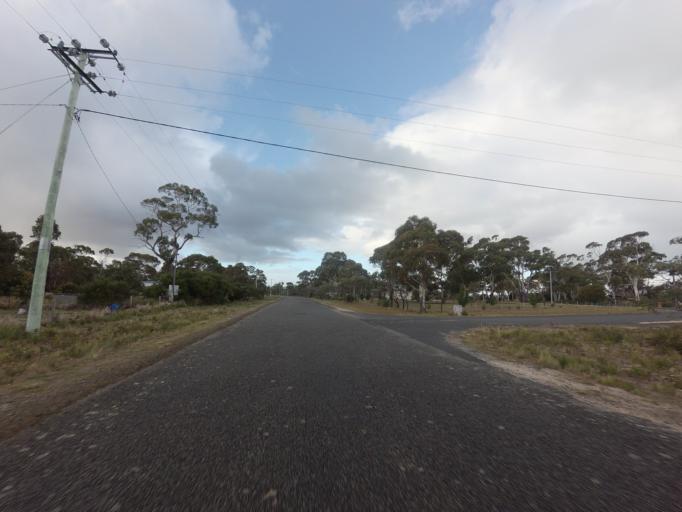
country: AU
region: Tasmania
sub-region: Break O'Day
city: St Helens
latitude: -42.1039
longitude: 148.0781
